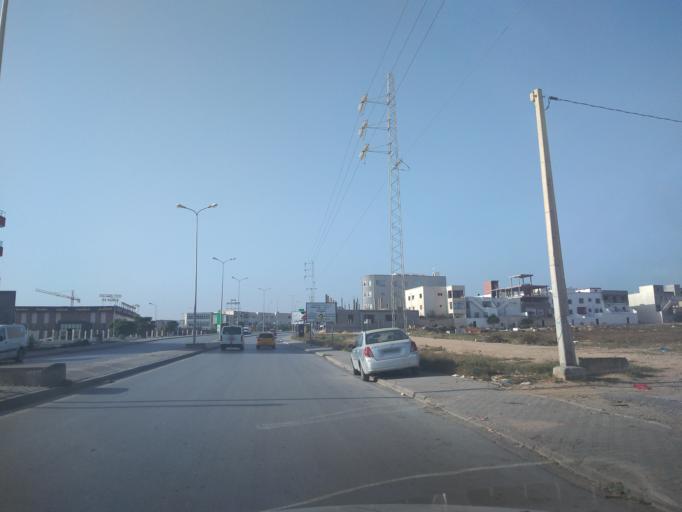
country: TN
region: Manouba
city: Manouba
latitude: 36.7868
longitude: 10.0830
